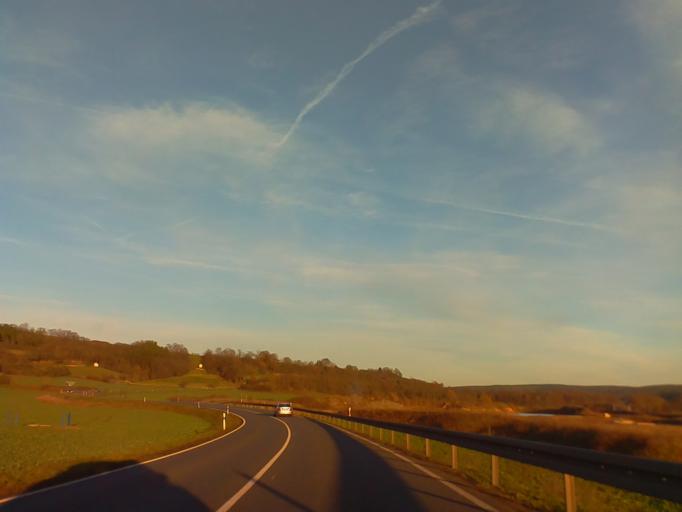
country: DE
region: Thuringia
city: Orlamunde
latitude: 50.7457
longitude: 11.4763
